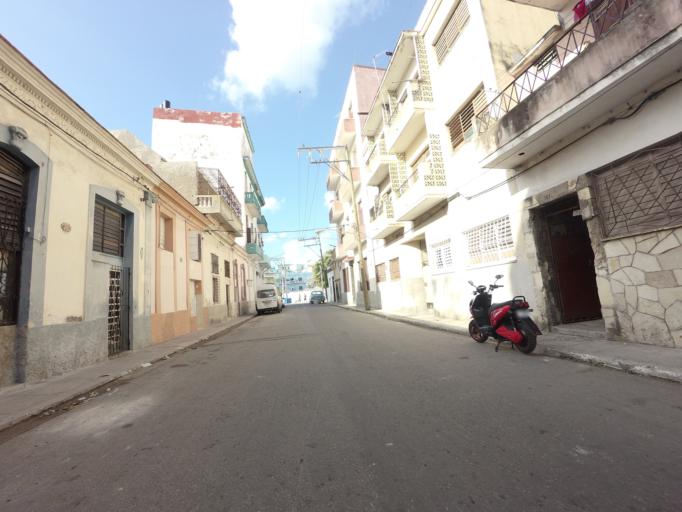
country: CU
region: La Habana
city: Havana
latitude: 23.1408
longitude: -82.3762
